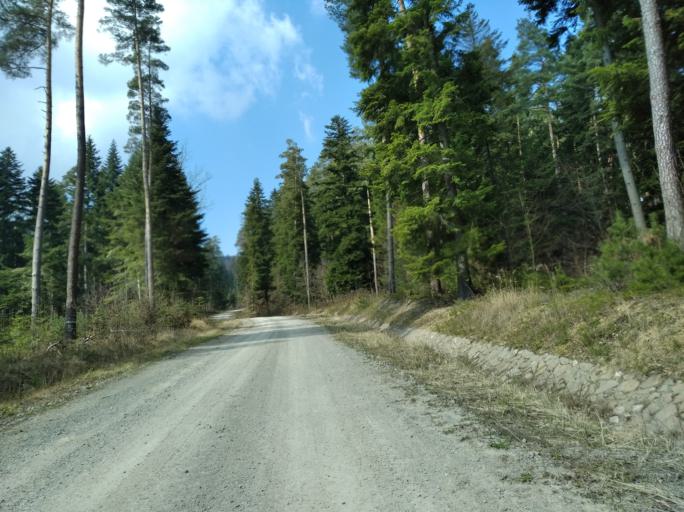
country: PL
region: Subcarpathian Voivodeship
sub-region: Powiat strzyzowski
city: Strzyzow
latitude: 49.8126
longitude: 21.8247
